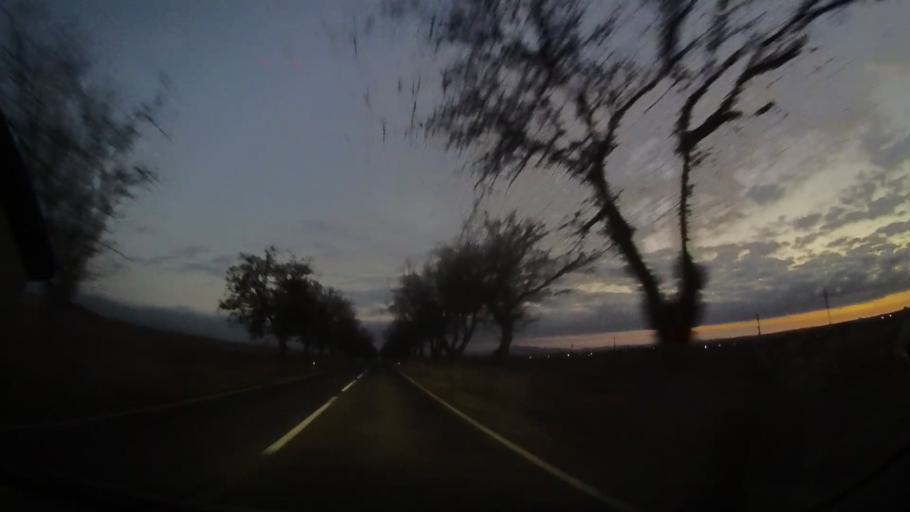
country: RO
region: Tulcea
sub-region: Comuna Frecatei
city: Cataloi
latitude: 45.1019
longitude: 28.7424
